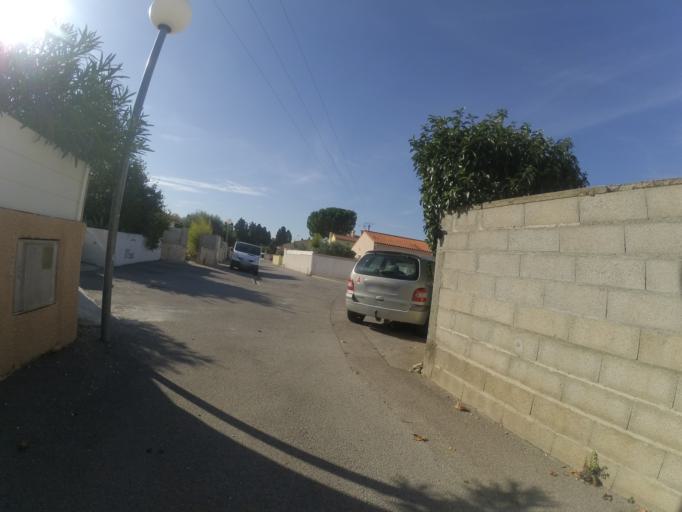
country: FR
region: Languedoc-Roussillon
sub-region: Departement des Pyrenees-Orientales
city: Pezilla-la-Riviere
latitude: 42.6954
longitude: 2.7630
